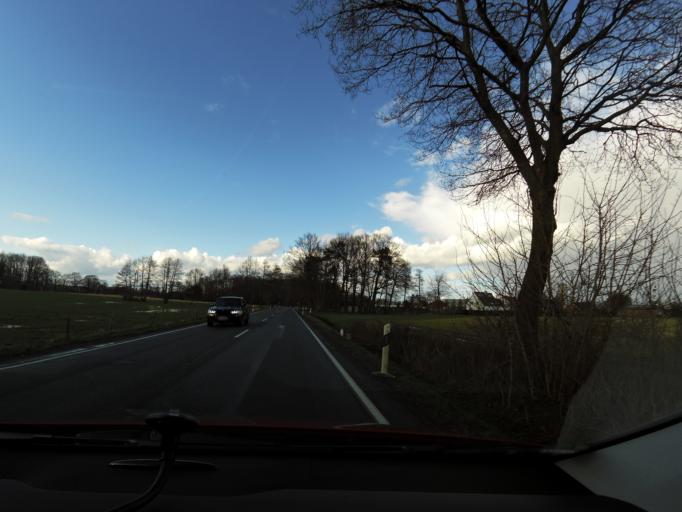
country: DE
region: North Rhine-Westphalia
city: Rietberg
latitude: 51.8697
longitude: 8.4524
